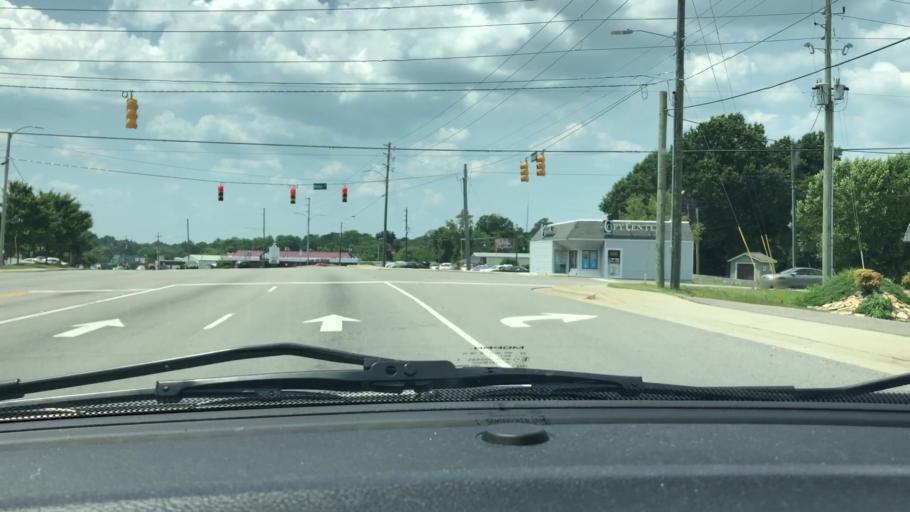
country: US
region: North Carolina
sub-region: Lee County
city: Sanford
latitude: 35.4700
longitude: -79.1665
